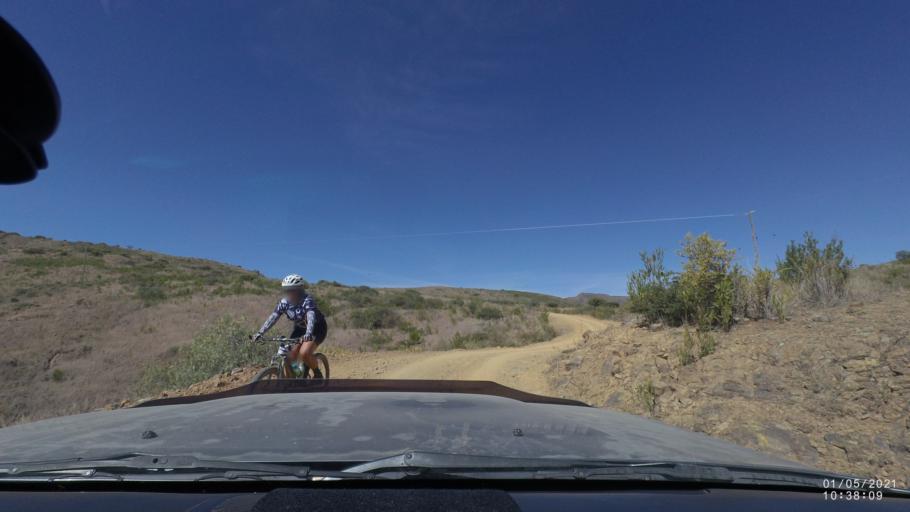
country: BO
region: Cochabamba
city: Capinota
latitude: -17.6033
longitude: -66.1852
